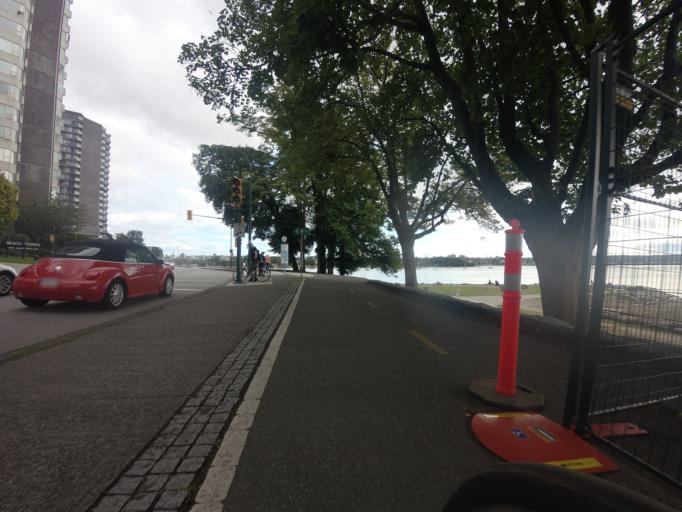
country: CA
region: British Columbia
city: West End
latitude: 49.2848
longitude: -123.1430
